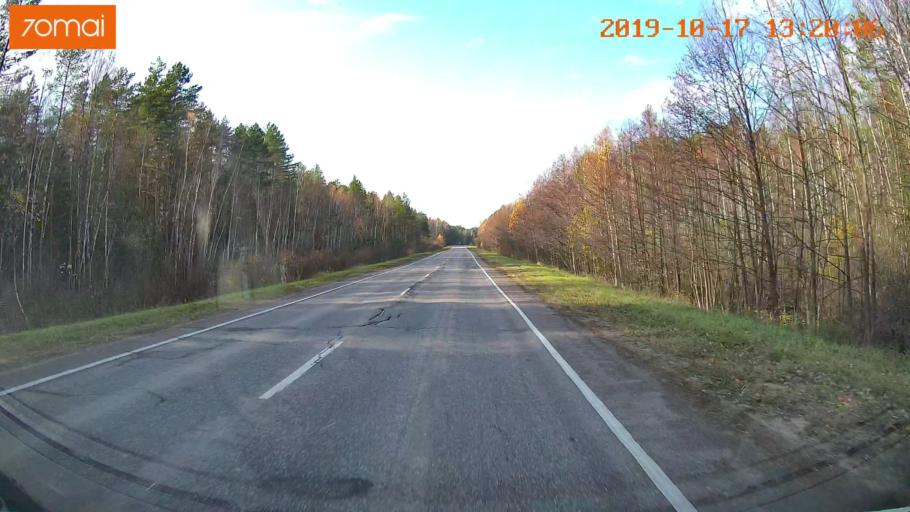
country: RU
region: Rjazan
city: Gus'-Zheleznyy
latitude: 55.0737
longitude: 41.0581
